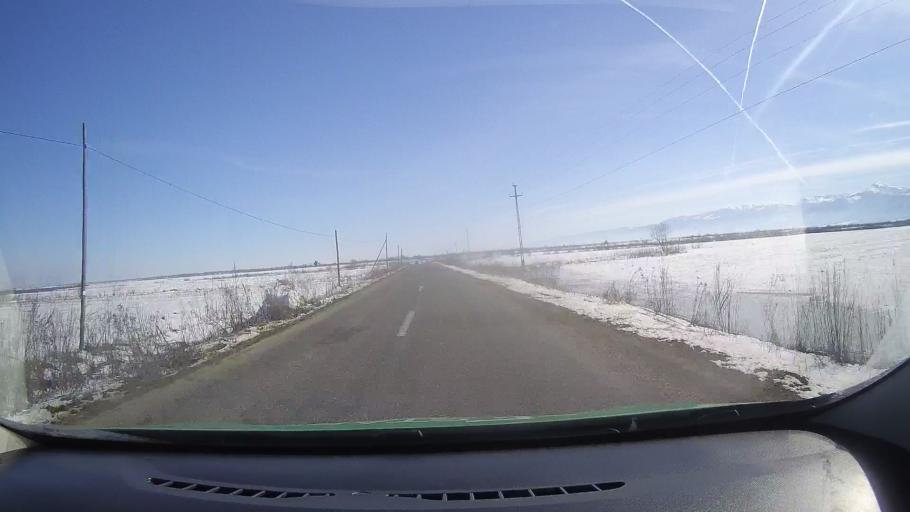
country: RO
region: Brasov
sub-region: Comuna Dragus
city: Dragus
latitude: 45.7629
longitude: 24.7971
